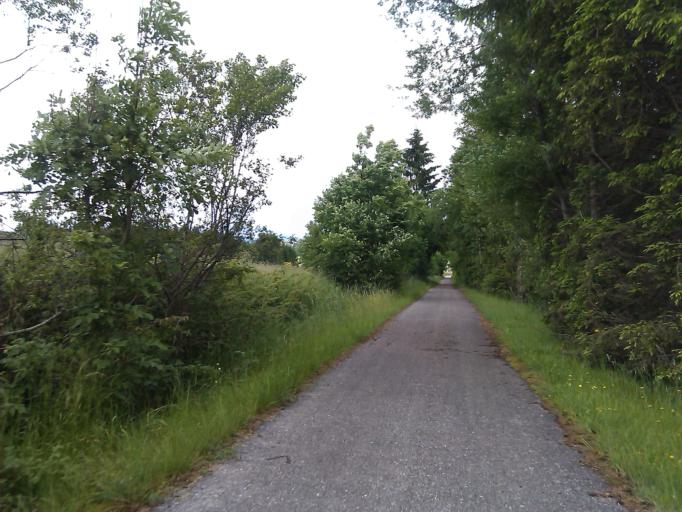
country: DE
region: Bavaria
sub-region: Swabia
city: Stotten am Auerberg
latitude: 47.7474
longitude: 10.6699
